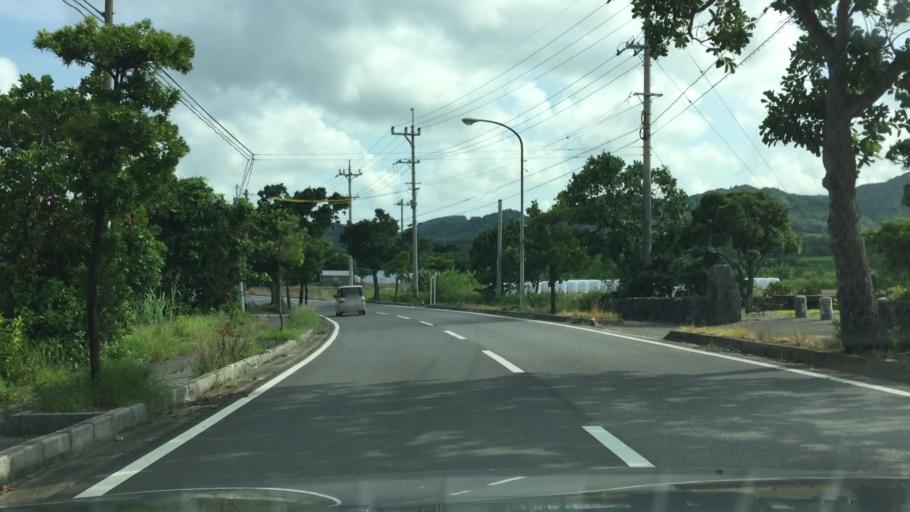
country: JP
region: Okinawa
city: Ishigaki
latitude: 24.4595
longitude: 124.2495
